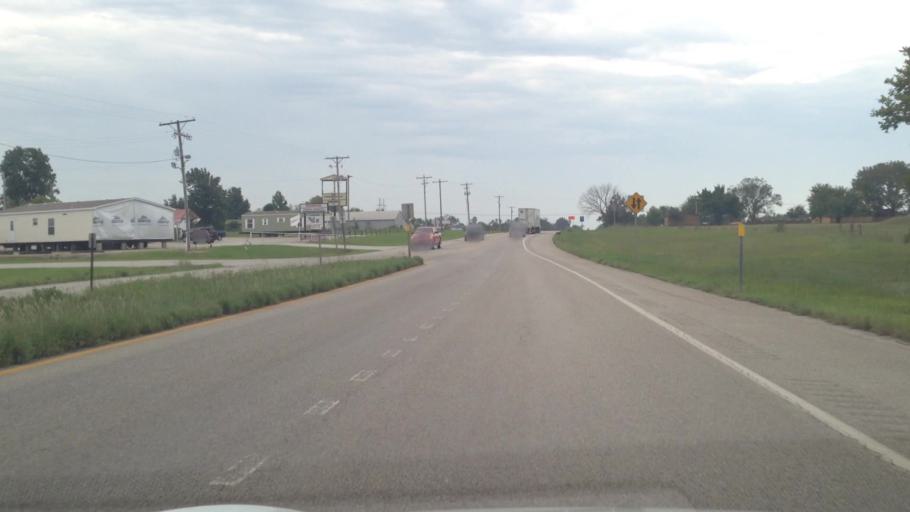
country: US
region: Kansas
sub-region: Crawford County
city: Pittsburg
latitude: 37.3373
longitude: -94.7055
